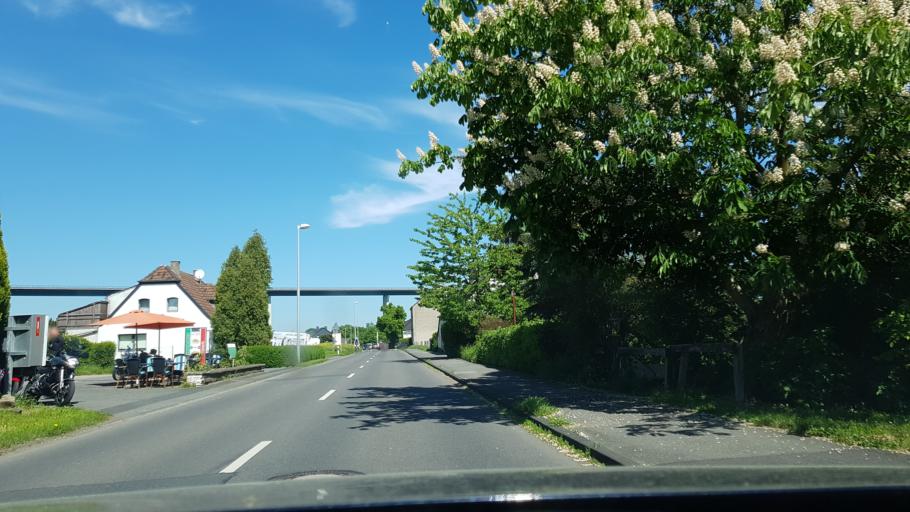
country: DE
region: North Rhine-Westphalia
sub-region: Regierungsbezirk Dusseldorf
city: Muelheim (Ruhr)
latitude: 51.3734
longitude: 6.9045
